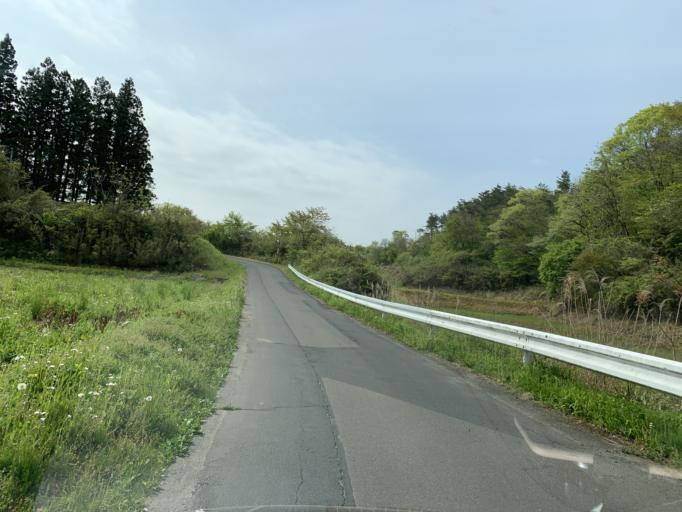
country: JP
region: Iwate
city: Ichinoseki
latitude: 38.9016
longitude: 141.0574
